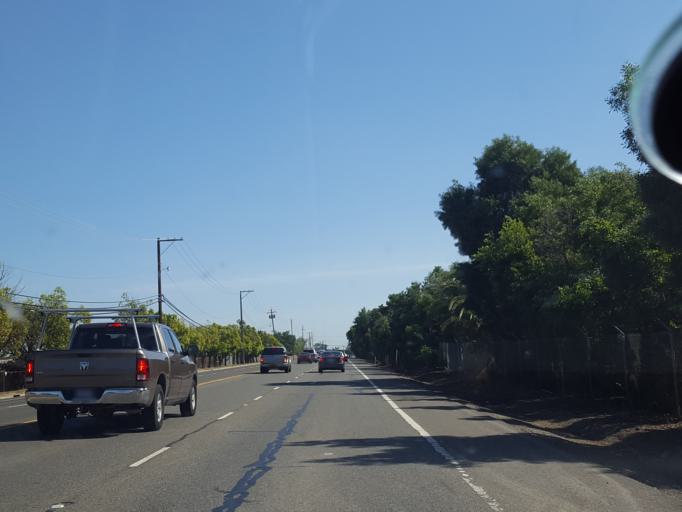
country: US
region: California
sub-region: Sacramento County
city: Rosemont
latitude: 38.5346
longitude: -121.3350
